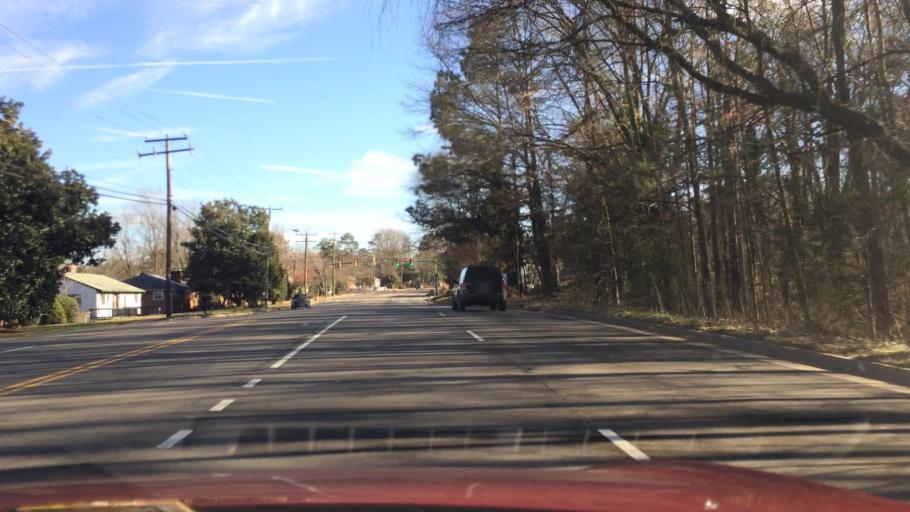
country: US
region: Virginia
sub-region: City of Richmond
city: Richmond
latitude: 37.5303
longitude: -77.5042
